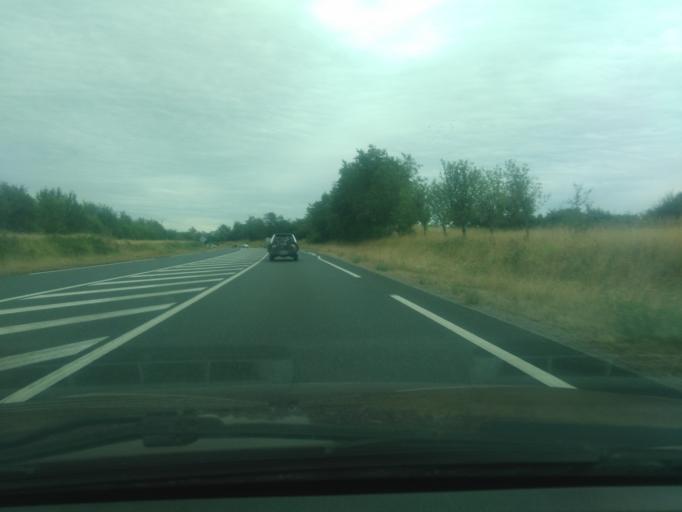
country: FR
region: Centre
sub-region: Departement de l'Indre
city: Le Pechereau
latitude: 46.5936
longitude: 1.5511
